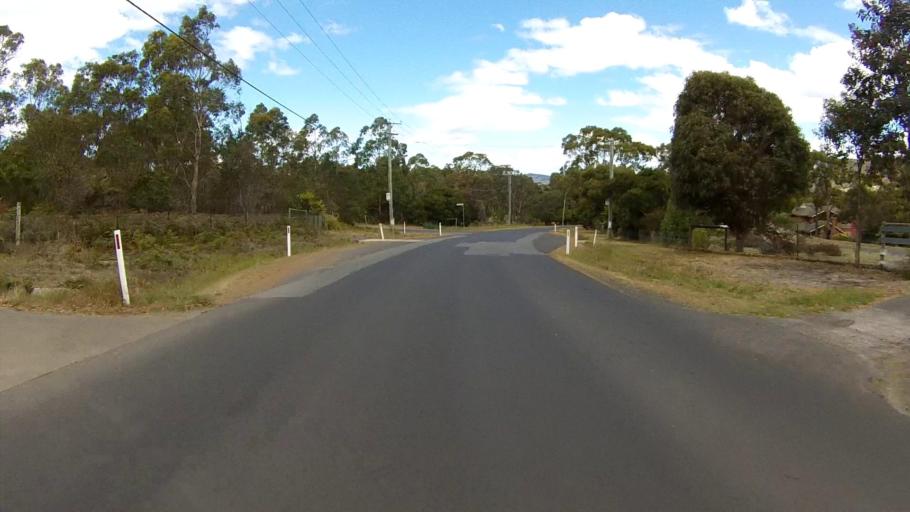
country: AU
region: Tasmania
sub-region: Clarence
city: Acton Park
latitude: -42.8768
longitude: 147.4904
